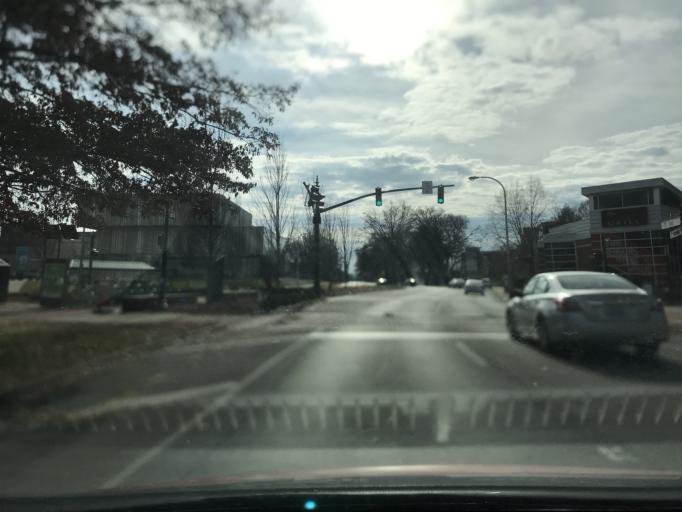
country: US
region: Kentucky
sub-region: Jefferson County
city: Louisville
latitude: 38.2195
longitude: -85.7614
